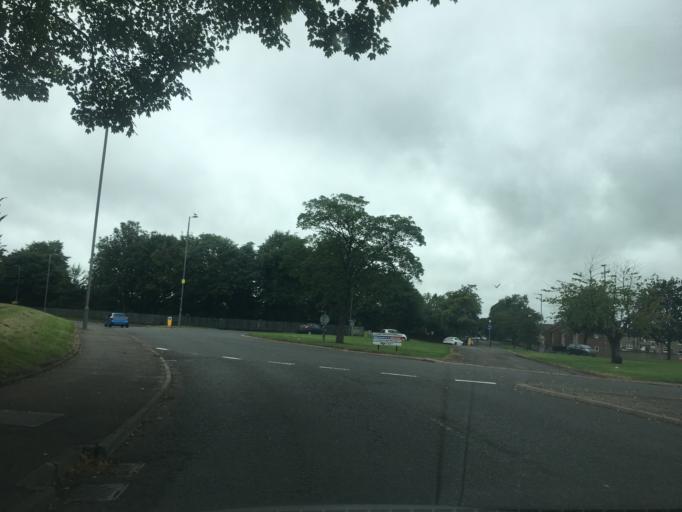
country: GB
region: Scotland
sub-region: Renfrewshire
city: Renfrew
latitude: 55.8744
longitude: -4.3783
